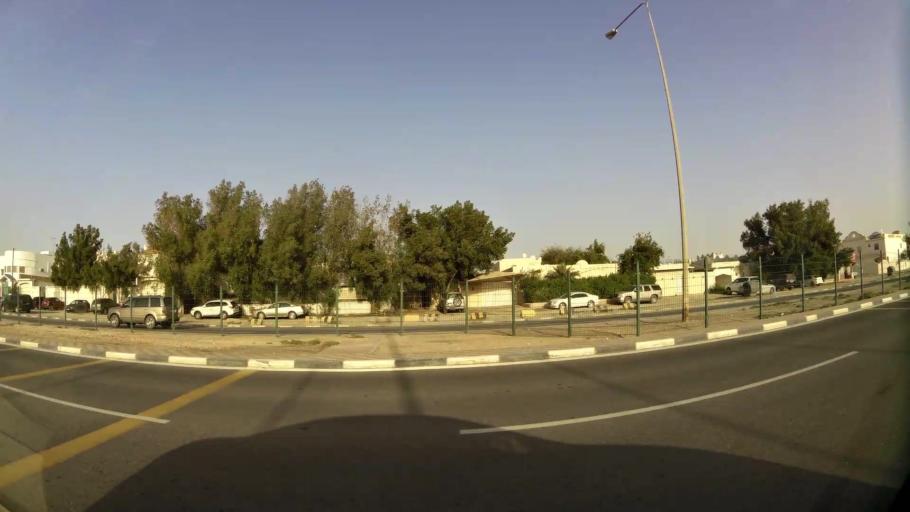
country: QA
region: Baladiyat ar Rayyan
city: Ar Rayyan
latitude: 25.3146
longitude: 51.4602
